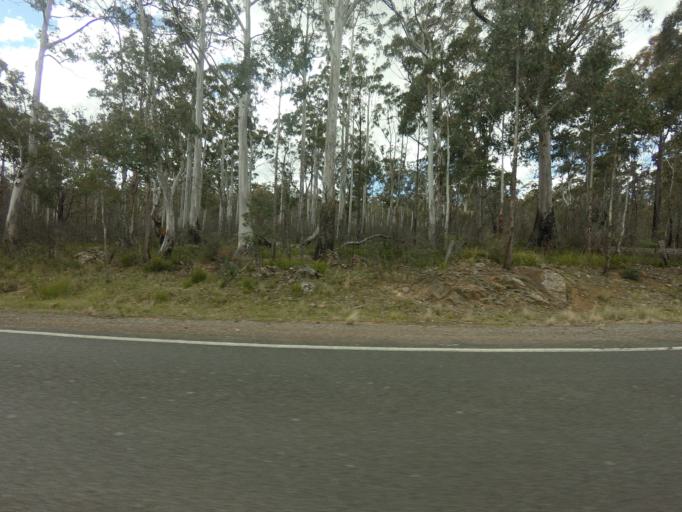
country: AU
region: Tasmania
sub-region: Northern Midlands
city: Evandale
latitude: -41.9905
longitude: 147.7092
